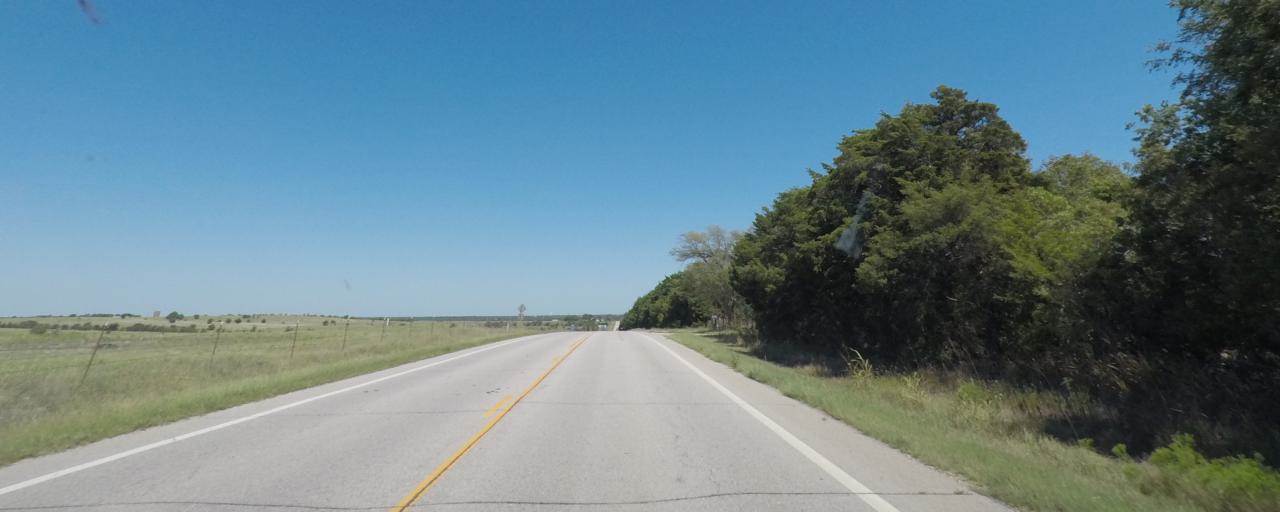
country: US
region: Kansas
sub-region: Sumner County
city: Wellington
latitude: 37.2177
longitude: -97.4023
